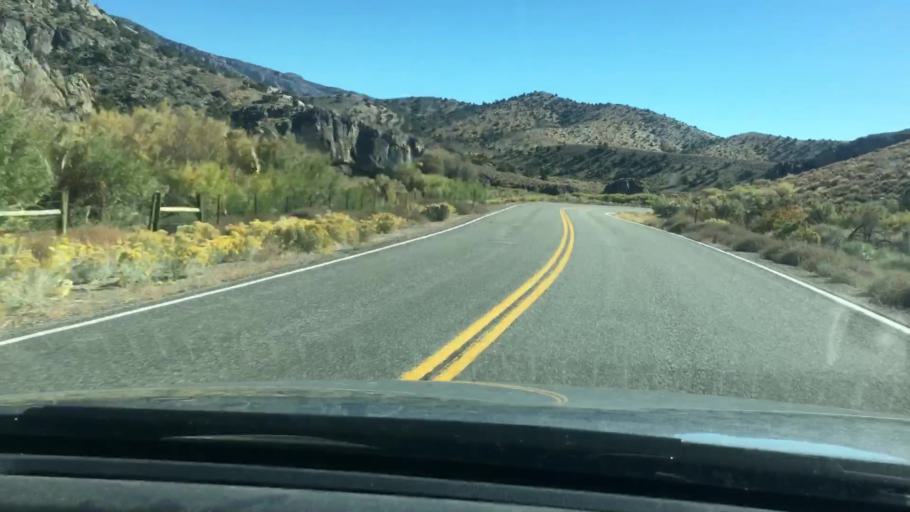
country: US
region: Nevada
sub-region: White Pine County
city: Ely
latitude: 38.7962
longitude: -115.3921
